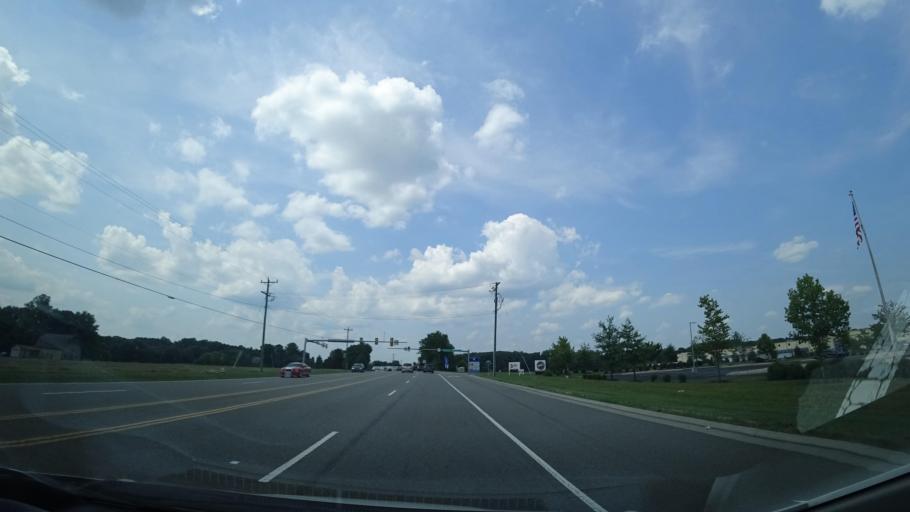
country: US
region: Virginia
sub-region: Hanover County
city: Ashland
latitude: 37.7847
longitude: -77.4659
